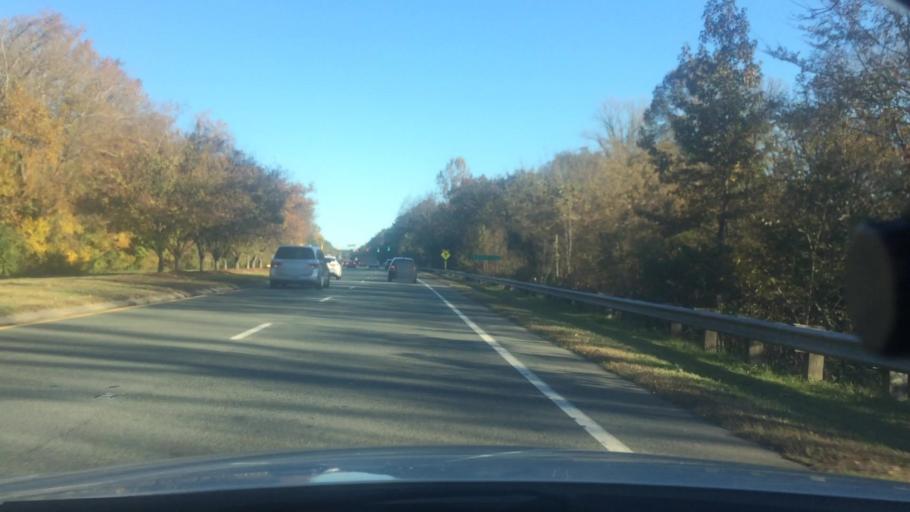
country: US
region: North Carolina
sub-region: Orange County
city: Chapel Hill
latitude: 35.9227
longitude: -79.0253
